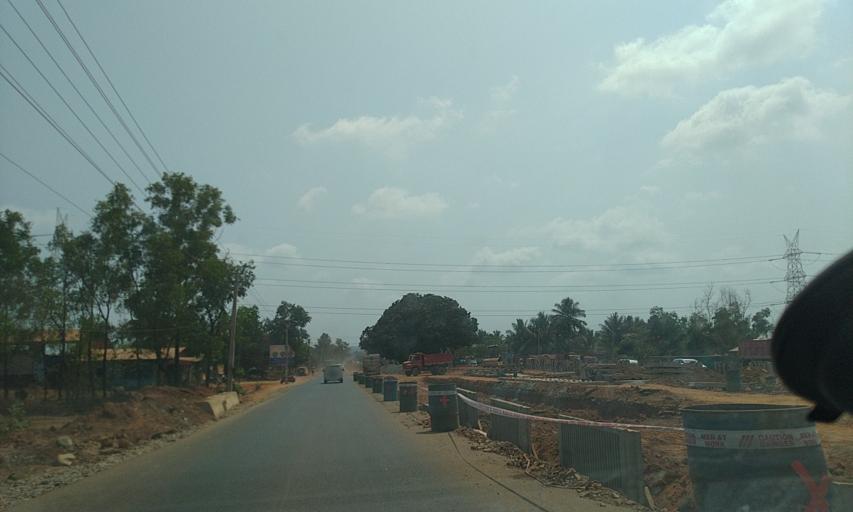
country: IN
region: Goa
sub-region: North Goa
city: Colovale
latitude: 15.6344
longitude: 73.8297
